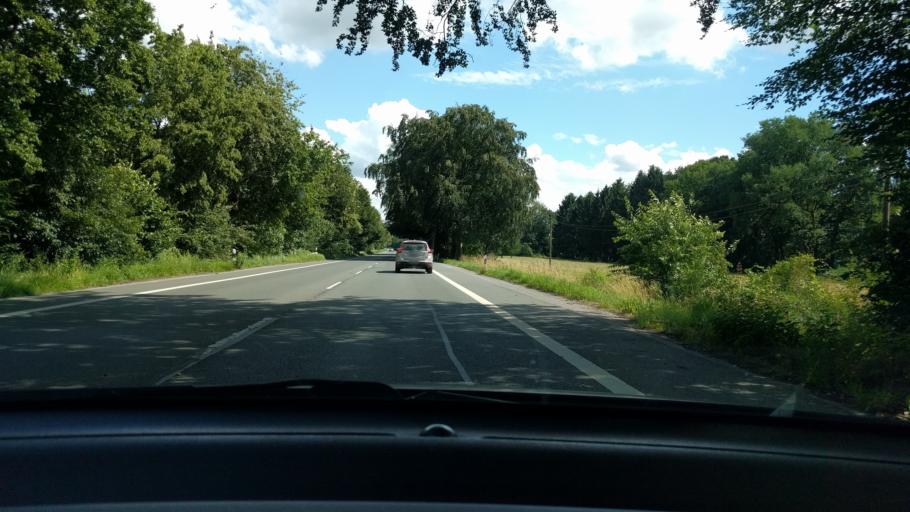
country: DE
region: North Rhine-Westphalia
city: Oer-Erkenschwick
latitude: 51.7058
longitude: 7.2958
